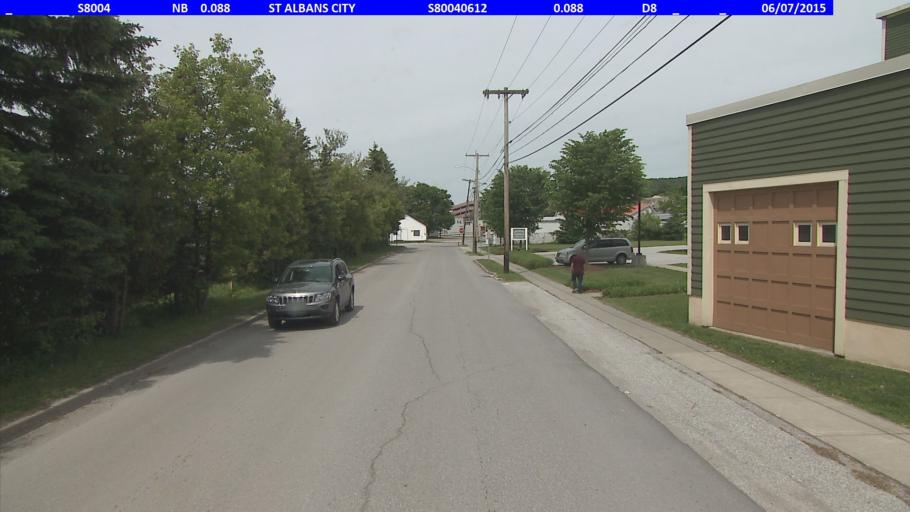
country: US
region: Vermont
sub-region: Franklin County
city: Saint Albans
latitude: 44.8086
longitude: -73.0869
